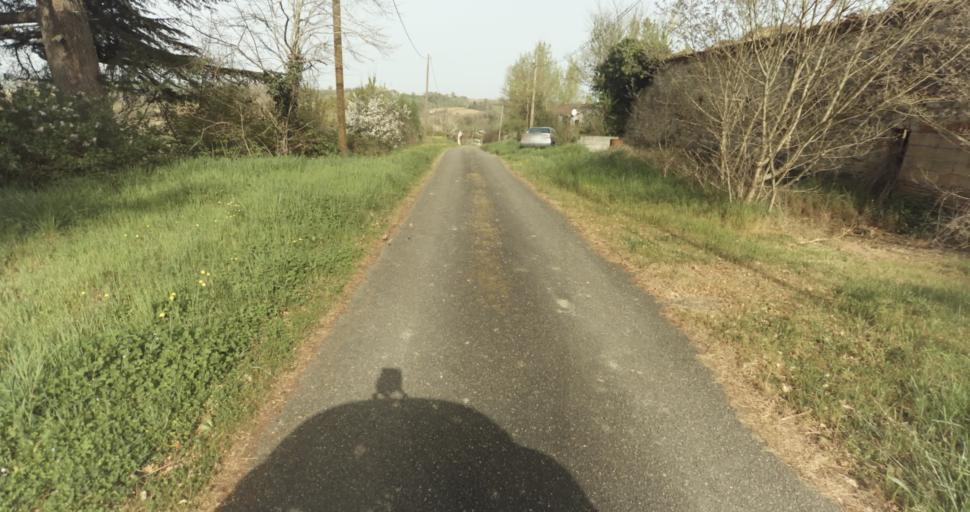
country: FR
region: Midi-Pyrenees
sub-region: Departement du Tarn-et-Garonne
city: Moissac
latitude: 44.1661
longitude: 1.0410
